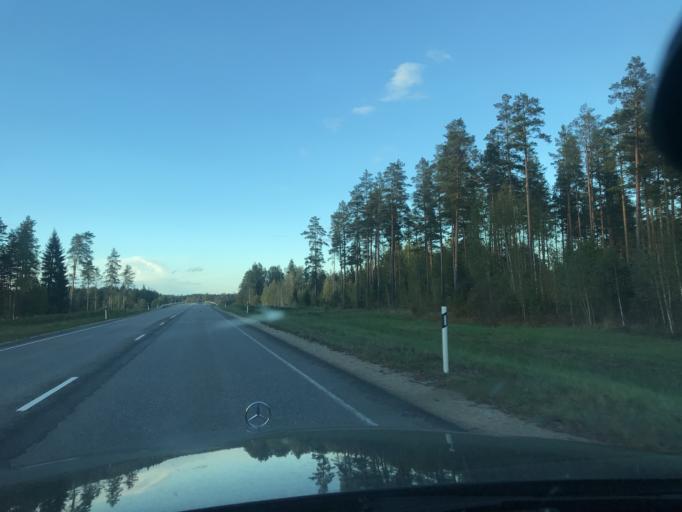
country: EE
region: Vorumaa
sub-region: Voru linn
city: Voru
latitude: 57.8217
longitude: 27.0641
